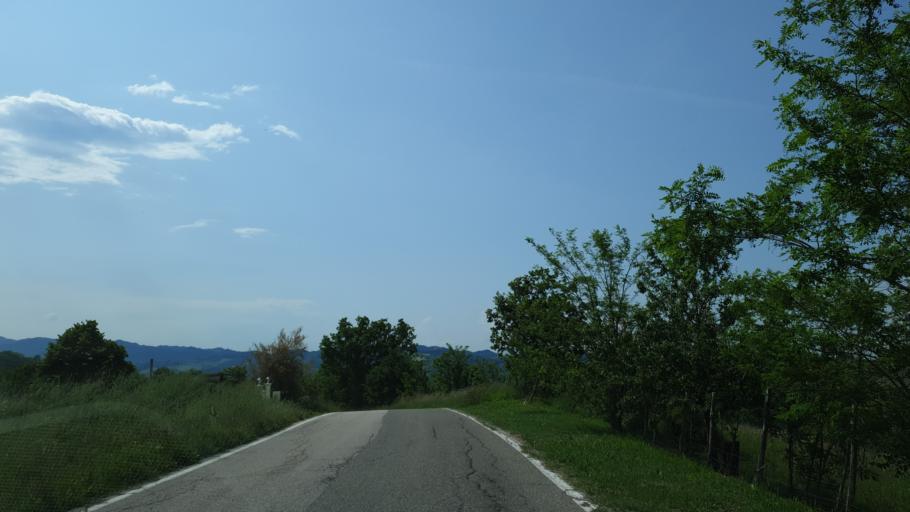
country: IT
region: Emilia-Romagna
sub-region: Provincia di Rimini
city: Sant'Agata Feltria
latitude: 43.9113
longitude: 12.2094
